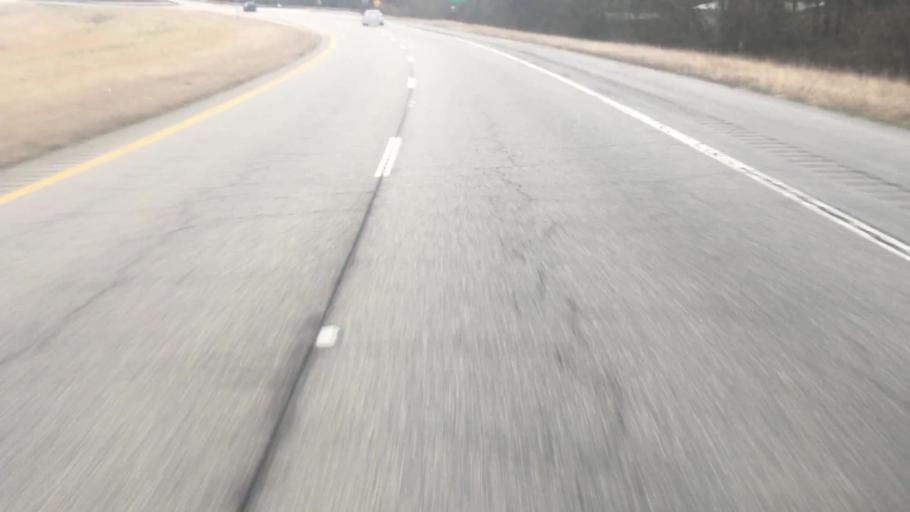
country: US
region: Alabama
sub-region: Walker County
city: Cordova
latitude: 33.8078
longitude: -87.1454
